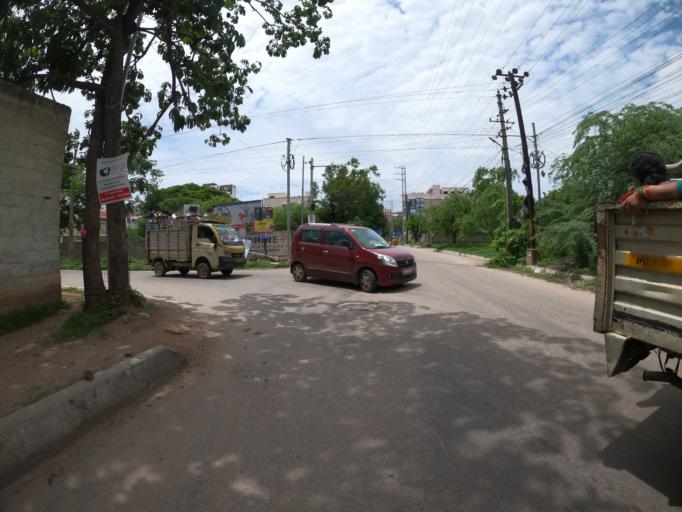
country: IN
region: Telangana
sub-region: Hyderabad
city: Hyderabad
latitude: 17.3684
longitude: 78.4131
